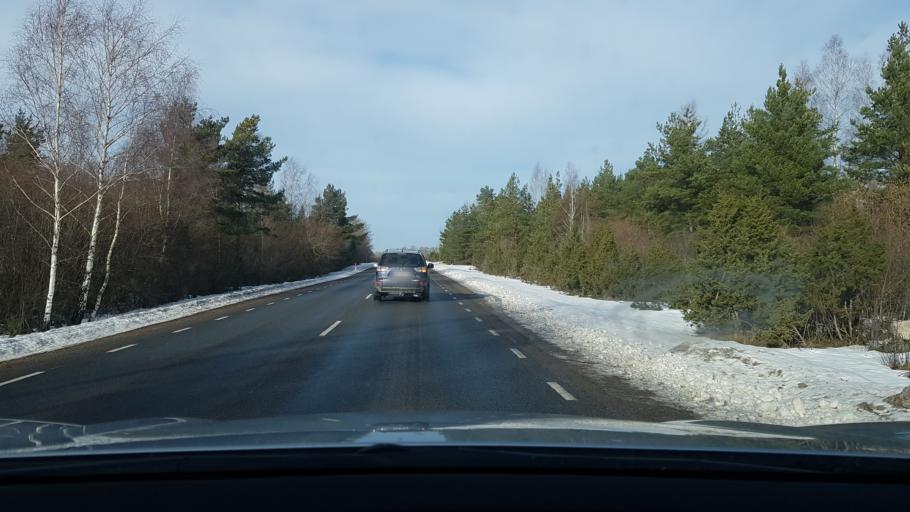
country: EE
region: Saare
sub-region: Kuressaare linn
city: Kuressaare
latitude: 58.2839
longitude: 22.5411
